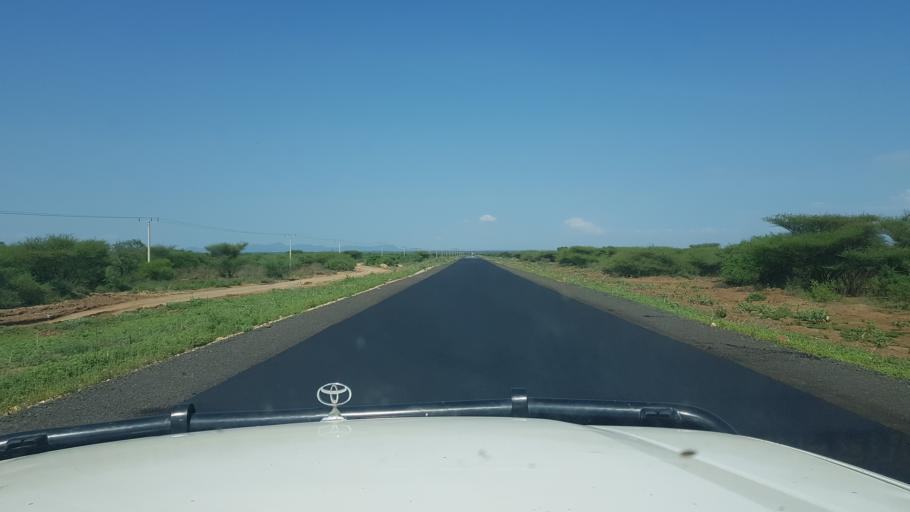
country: ET
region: Southern Nations, Nationalities, and People's Region
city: Lobuni
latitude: 5.1055
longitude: 36.1889
